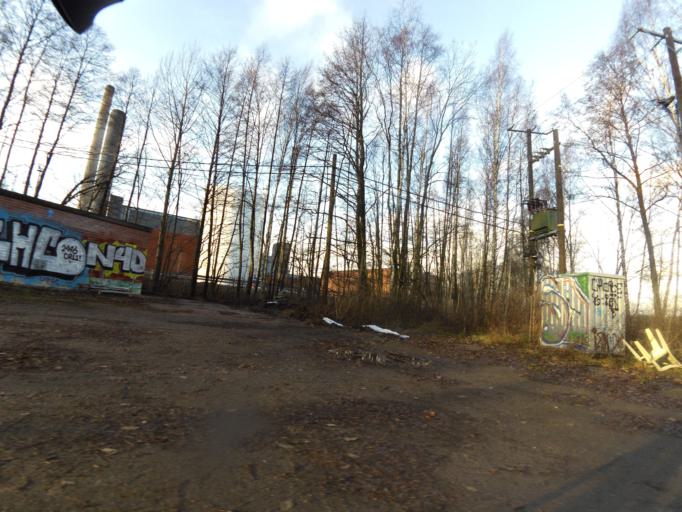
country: FI
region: Uusimaa
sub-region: Helsinki
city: Koukkuniemi
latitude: 60.1504
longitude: 24.7223
